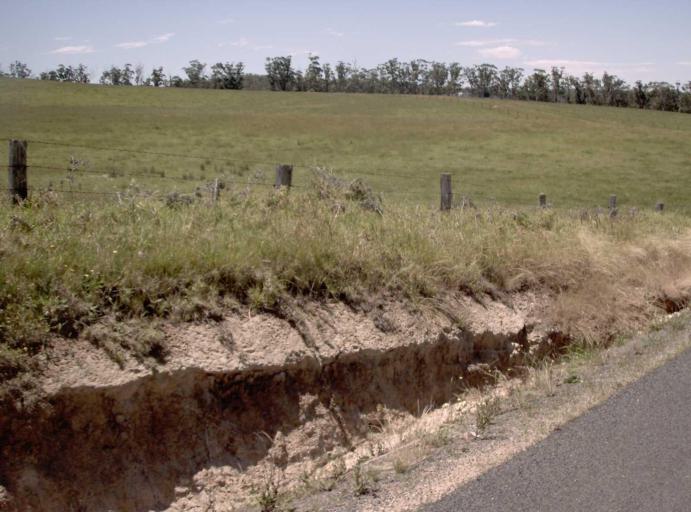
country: AU
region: Victoria
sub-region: East Gippsland
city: Lakes Entrance
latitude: -37.7047
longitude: 148.5279
